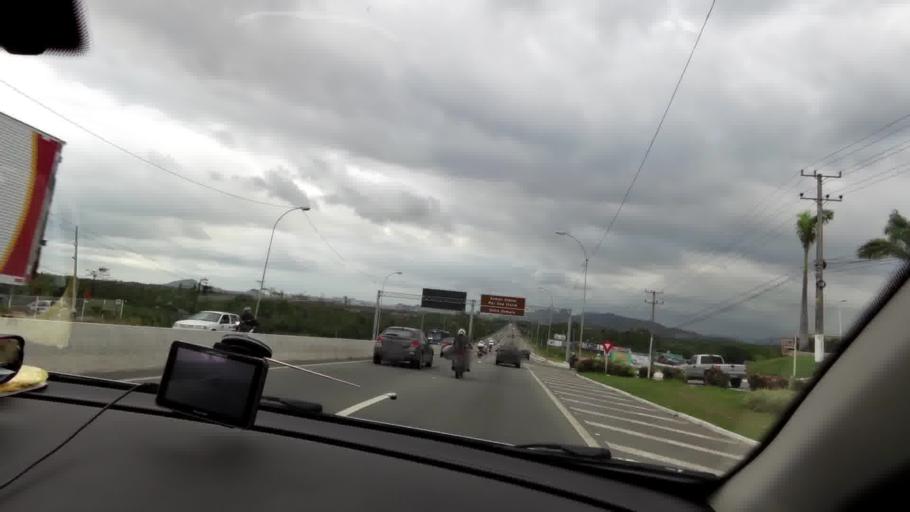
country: BR
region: Espirito Santo
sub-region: Vila Velha
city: Vila Velha
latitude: -20.2384
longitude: -40.2785
